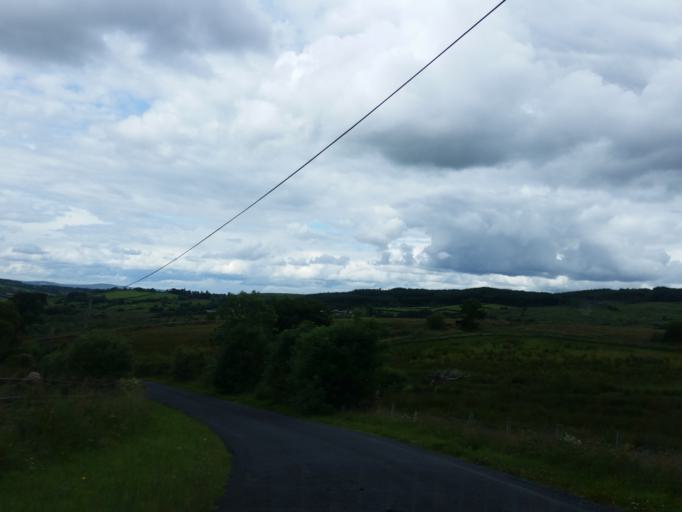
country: GB
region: Northern Ireland
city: Fivemiletown
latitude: 54.2871
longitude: -7.2765
